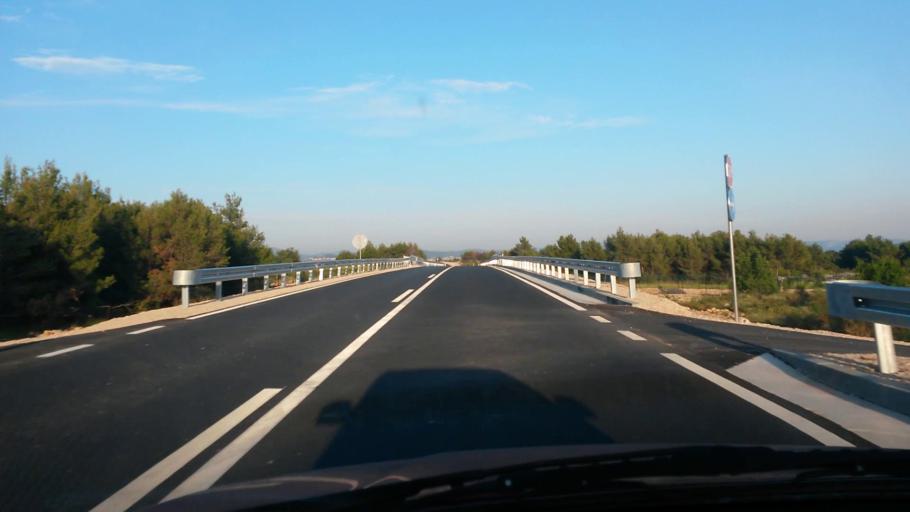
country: HR
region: Sibensko-Kniniska
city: Vodice
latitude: 43.7688
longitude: 15.7987
